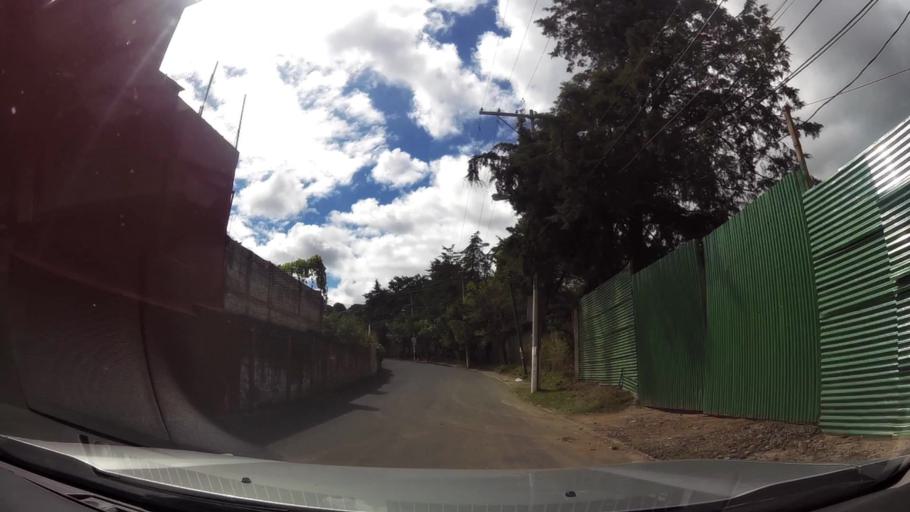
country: GT
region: Guatemala
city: Chinautla
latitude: 14.6867
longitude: -90.5441
